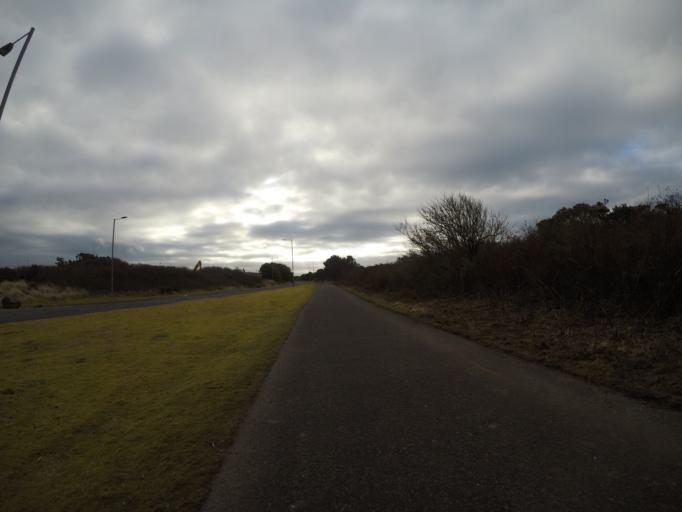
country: GB
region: Scotland
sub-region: North Ayrshire
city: Irvine
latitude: 55.5997
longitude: -4.6789
